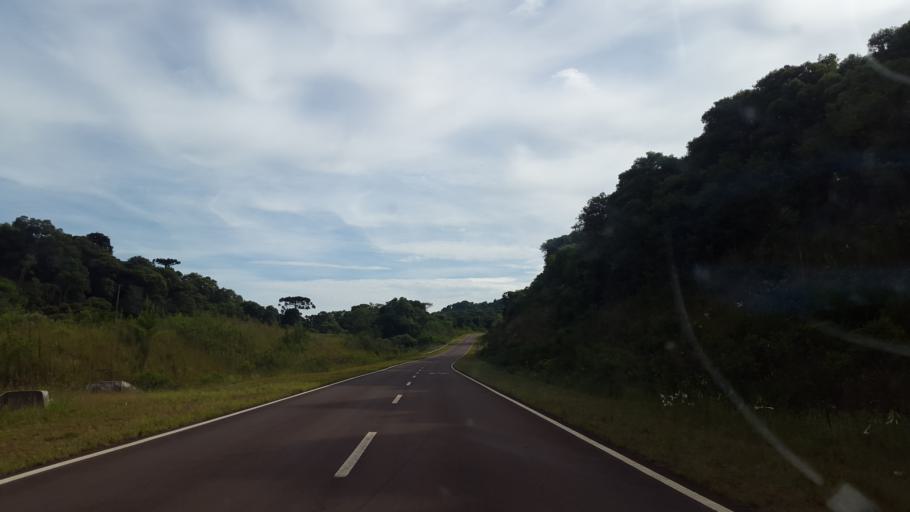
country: AR
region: Misiones
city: Bernardo de Irigoyen
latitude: -26.3260
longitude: -53.7577
